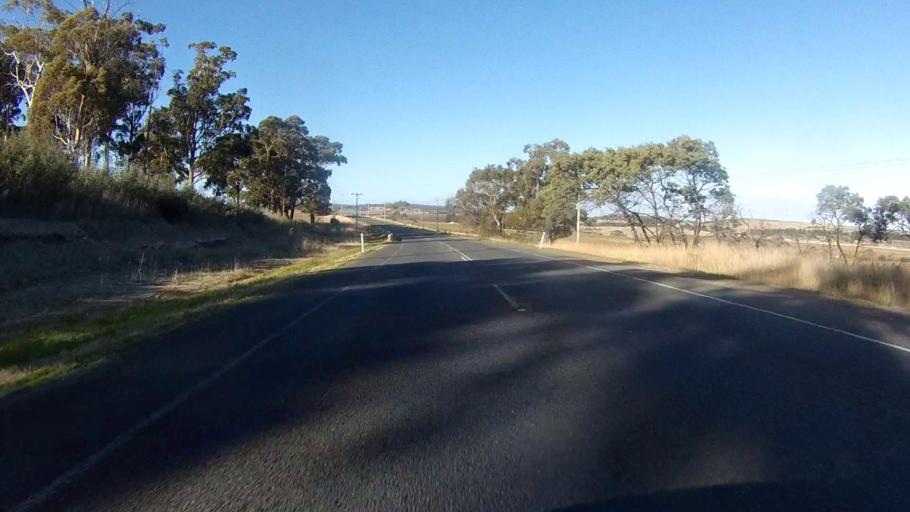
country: AU
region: Tasmania
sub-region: Sorell
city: Sorell
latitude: -42.7933
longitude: 147.6079
